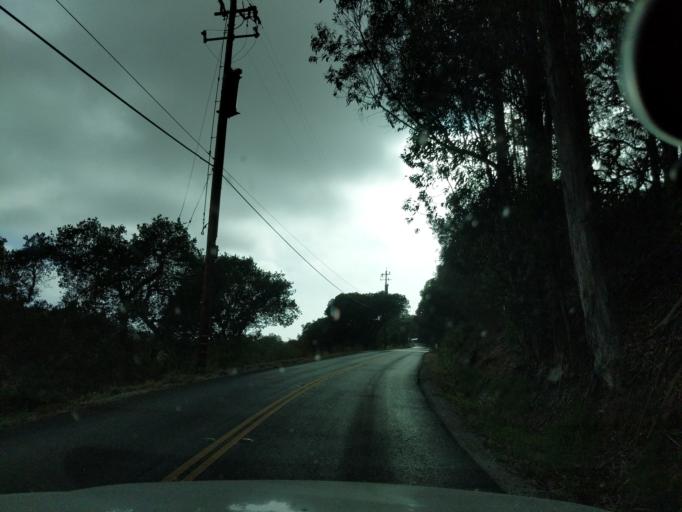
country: US
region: California
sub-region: Monterey County
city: Elkhorn
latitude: 36.8155
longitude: -121.7252
